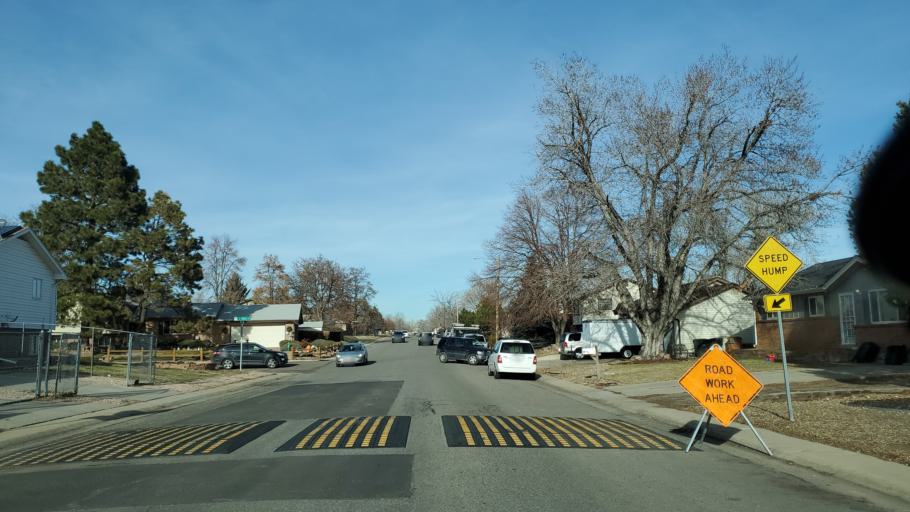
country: US
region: Colorado
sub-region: Adams County
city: Northglenn
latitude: 39.9052
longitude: -104.9607
